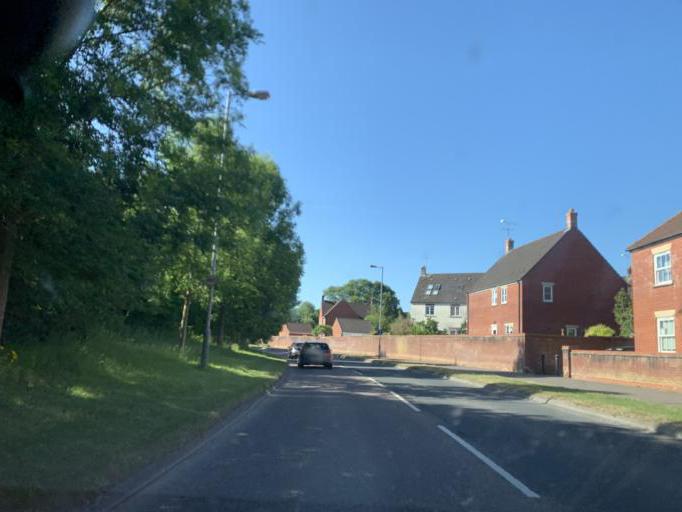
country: GB
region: England
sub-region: Wiltshire
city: Devizes
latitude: 51.3480
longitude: -1.9724
